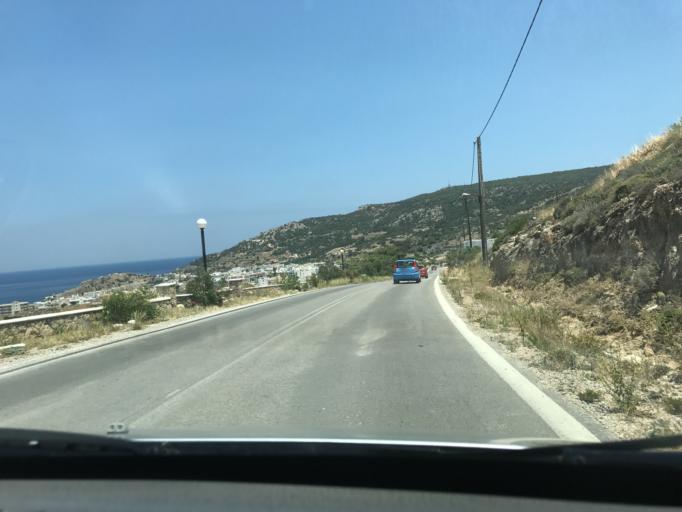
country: GR
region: South Aegean
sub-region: Nomos Dodekanisou
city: Karpathos
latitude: 35.5002
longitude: 27.2036
